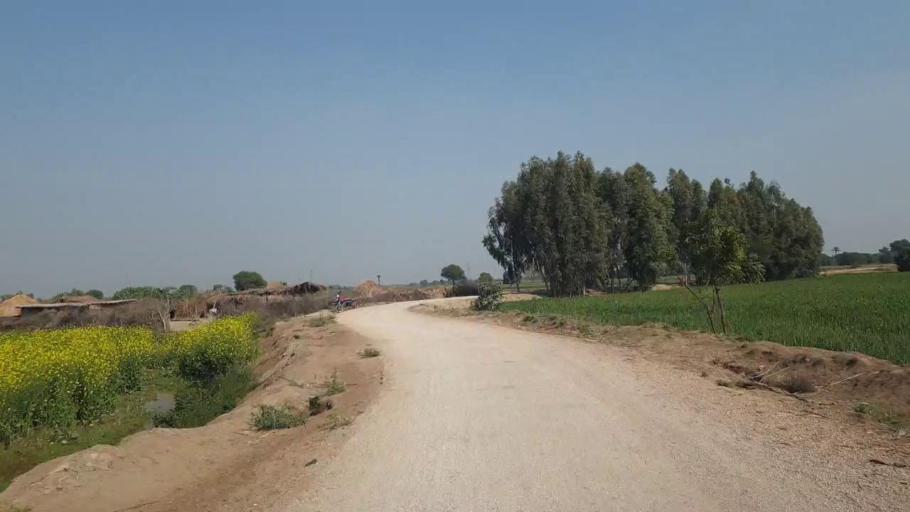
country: PK
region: Sindh
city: Chambar
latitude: 25.3518
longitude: 68.9023
